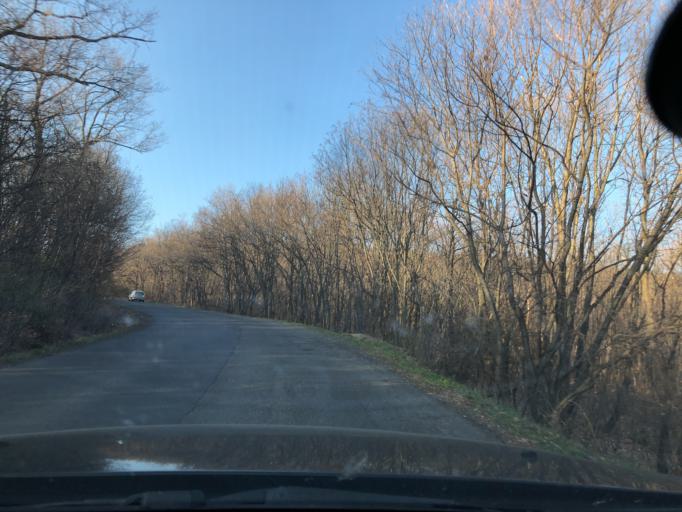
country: HU
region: Nograd
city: Paszto
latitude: 47.9220
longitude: 19.6317
